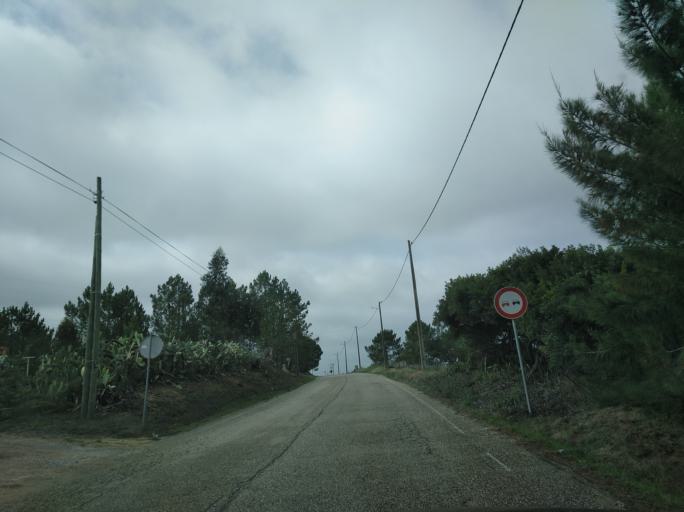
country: PT
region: Setubal
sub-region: Santiago do Cacem
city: Santo Andre
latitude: 38.1369
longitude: -8.7561
